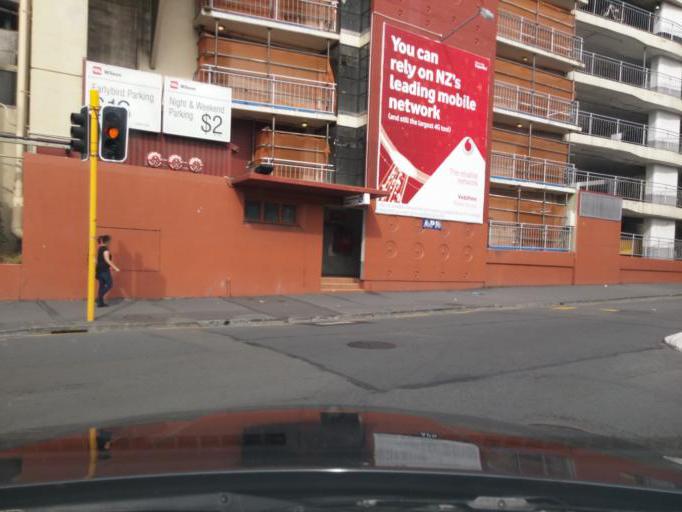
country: NZ
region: Wellington
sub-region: Wellington City
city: Wellington
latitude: -41.2844
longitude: 174.7742
